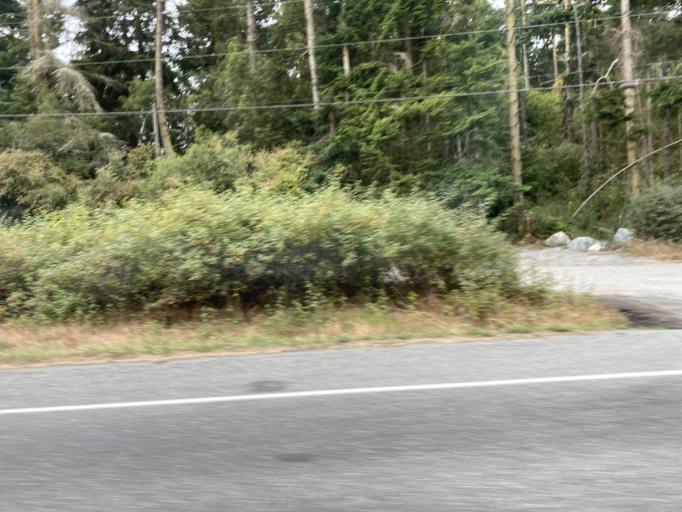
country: US
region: Washington
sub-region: Island County
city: Coupeville
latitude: 48.2319
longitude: -122.7402
